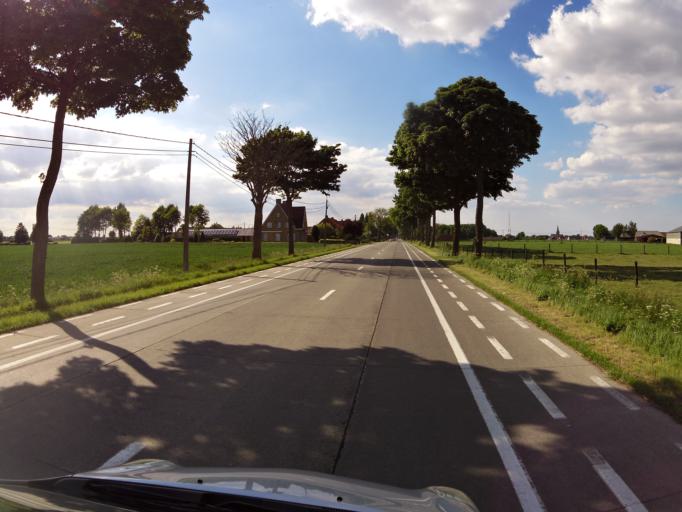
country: BE
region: Flanders
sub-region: Provincie West-Vlaanderen
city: Poperinge
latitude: 50.9238
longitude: 2.7503
